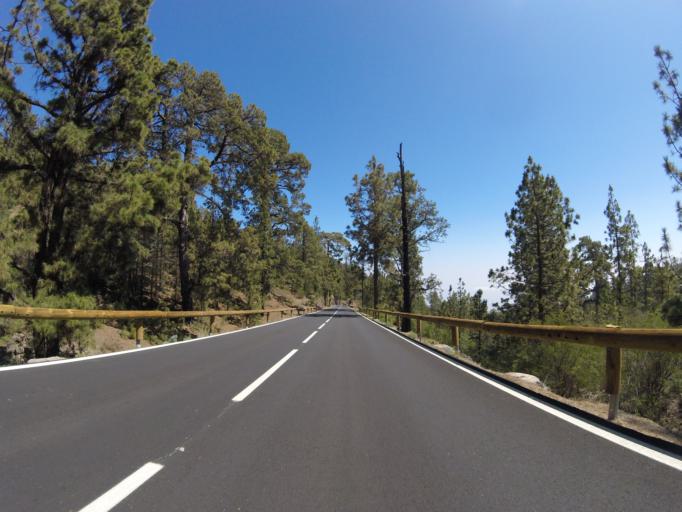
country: ES
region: Canary Islands
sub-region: Provincia de Santa Cruz de Tenerife
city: Vilaflor
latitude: 28.1741
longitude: -16.6383
